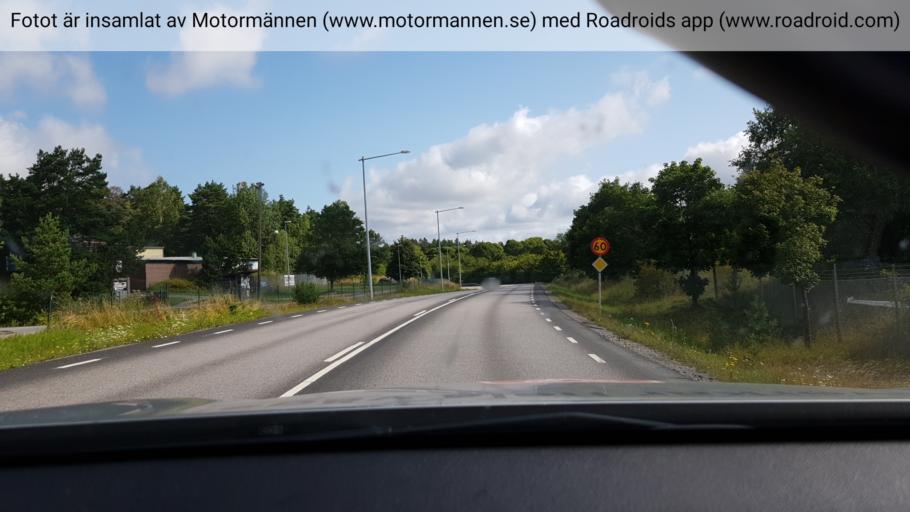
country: SE
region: Uppsala
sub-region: Knivsta Kommun
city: Knivsta
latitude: 59.7241
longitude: 17.7763
